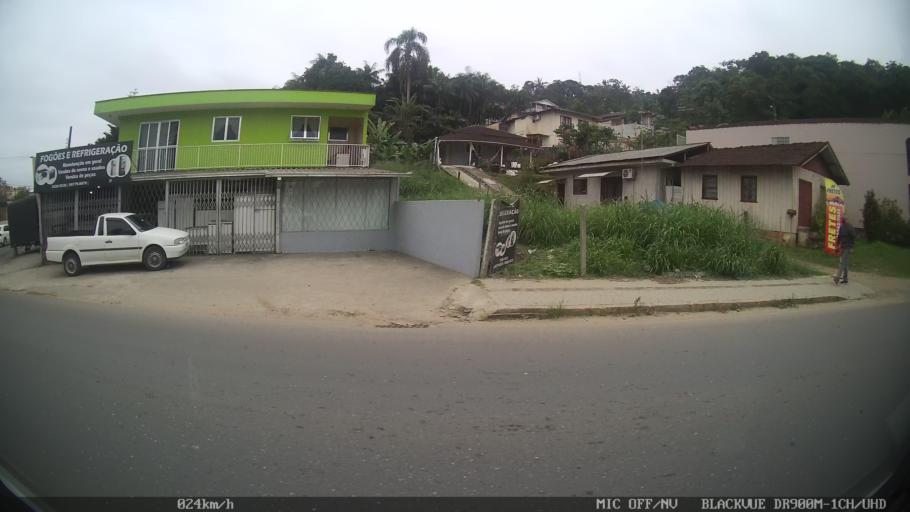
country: BR
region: Santa Catarina
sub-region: Joinville
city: Joinville
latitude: -26.3350
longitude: -48.8291
